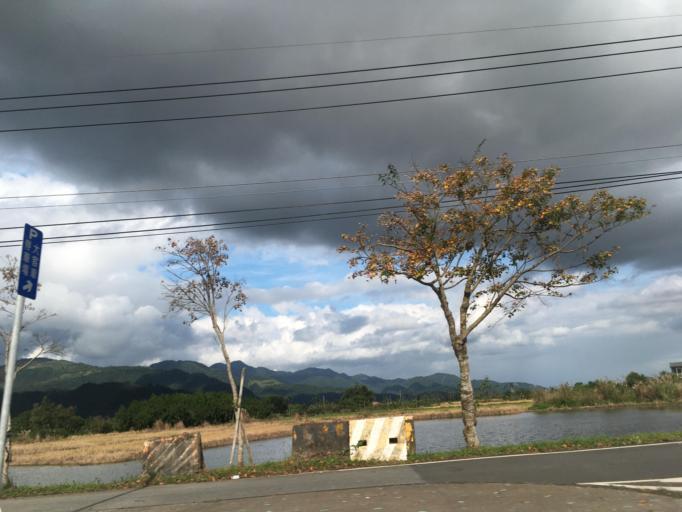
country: TW
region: Taiwan
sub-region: Yilan
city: Yilan
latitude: 24.6659
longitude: 121.6163
